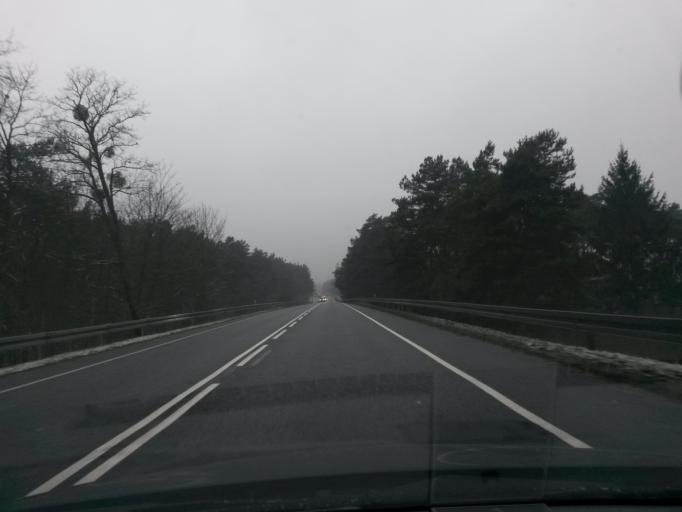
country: PL
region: Kujawsko-Pomorskie
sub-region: Powiat torunski
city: Wielka Nieszawka
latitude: 52.9881
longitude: 18.4790
